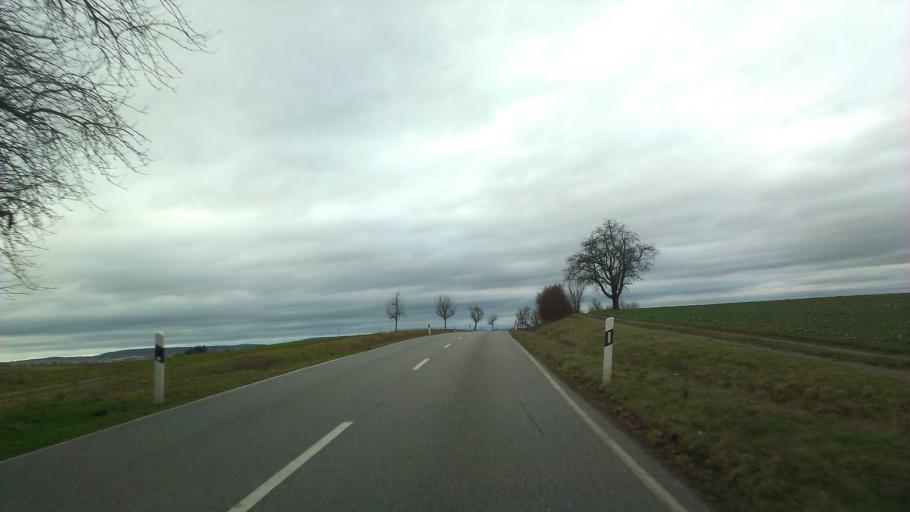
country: DE
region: Baden-Wuerttemberg
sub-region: Regierungsbezirk Stuttgart
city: Eppingen
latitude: 49.1076
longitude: 8.8999
